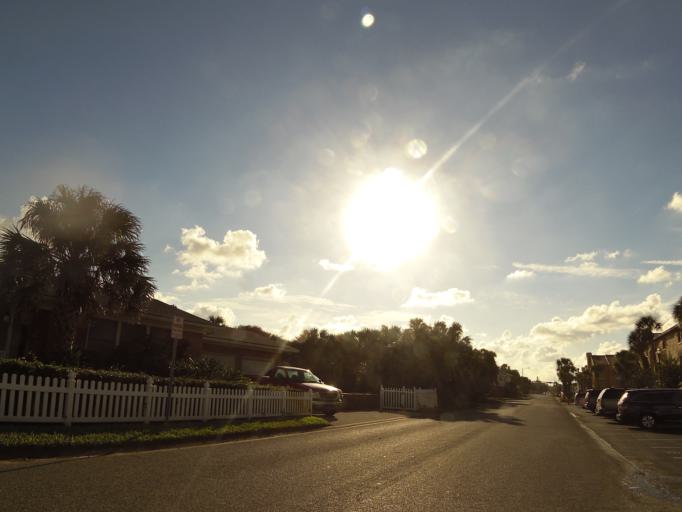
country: US
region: Florida
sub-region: Saint Johns County
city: Ponte Vedra Beach
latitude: 30.2676
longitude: -81.3855
